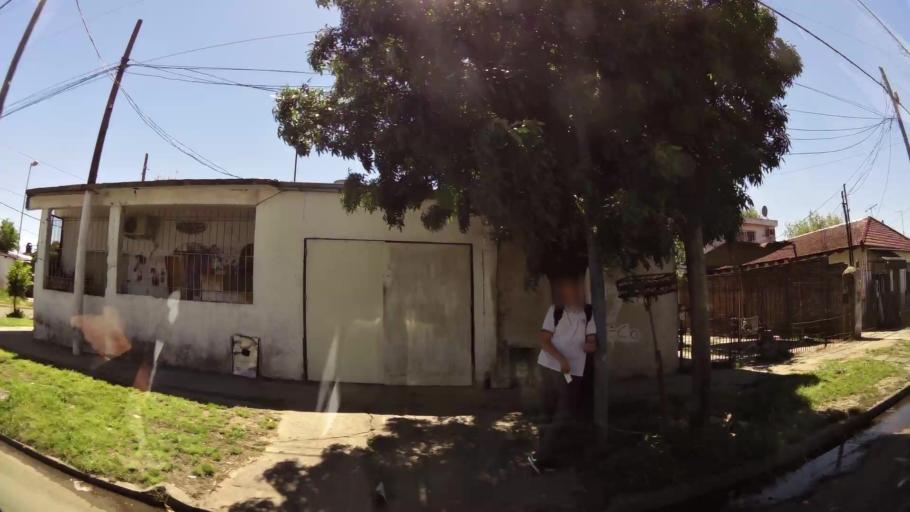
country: AR
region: Buenos Aires
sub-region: Partido de Lanus
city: Lanus
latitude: -34.7335
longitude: -58.3406
